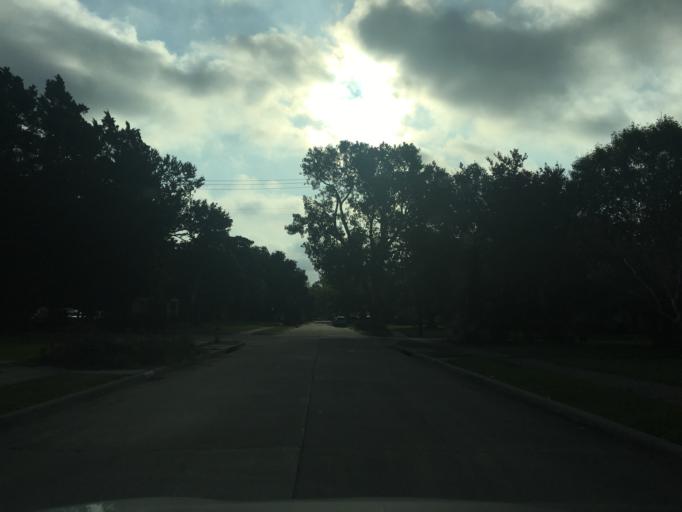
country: US
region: Texas
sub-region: Dallas County
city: Highland Park
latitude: 32.8460
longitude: -96.7504
